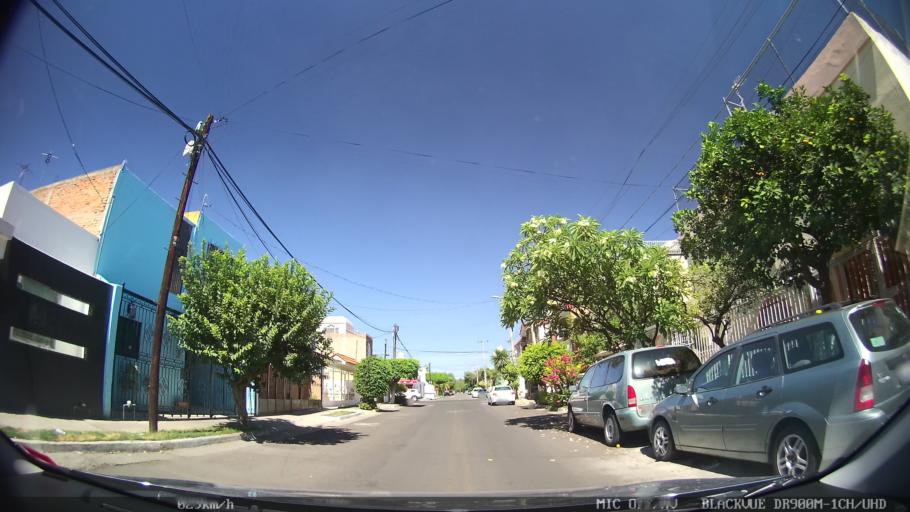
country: MX
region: Jalisco
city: Tlaquepaque
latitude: 20.6467
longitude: -103.2955
